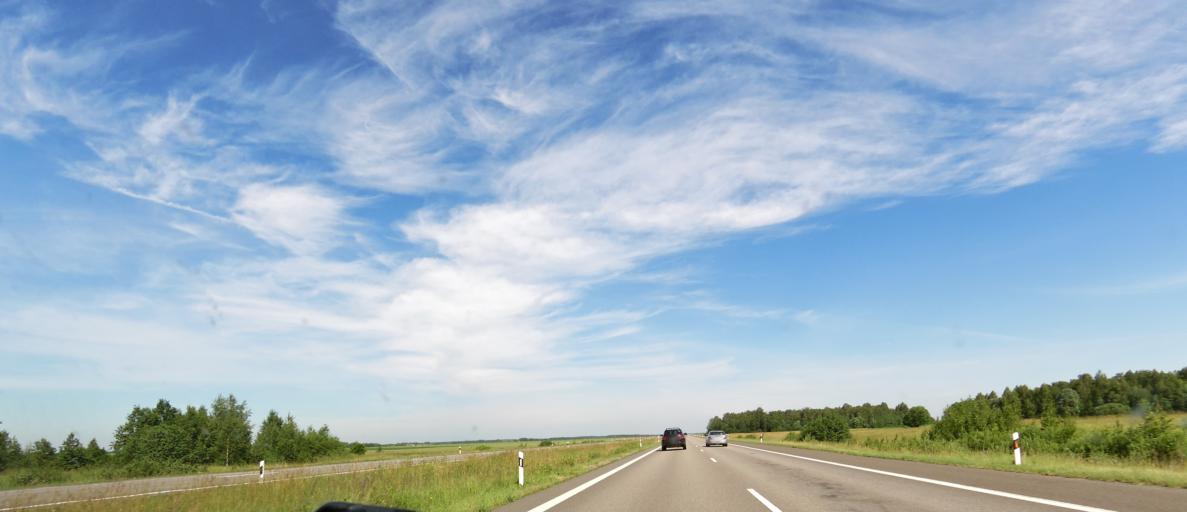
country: LT
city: Ramygala
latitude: 55.5832
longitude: 24.4598
